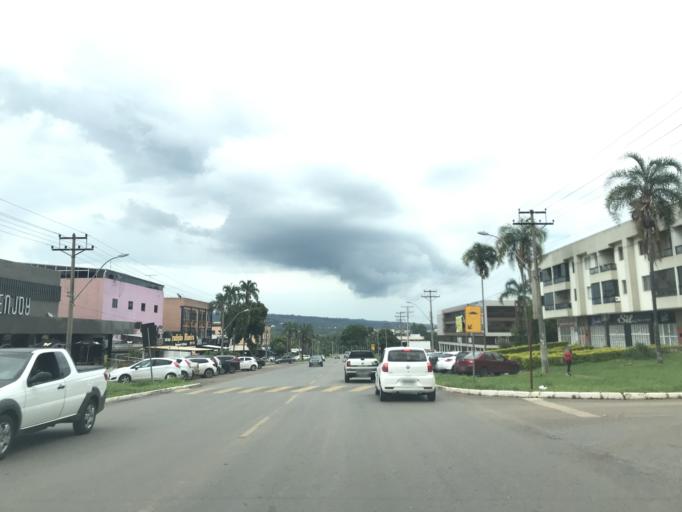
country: BR
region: Federal District
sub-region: Brasilia
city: Brasilia
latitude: -15.6558
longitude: -47.8089
